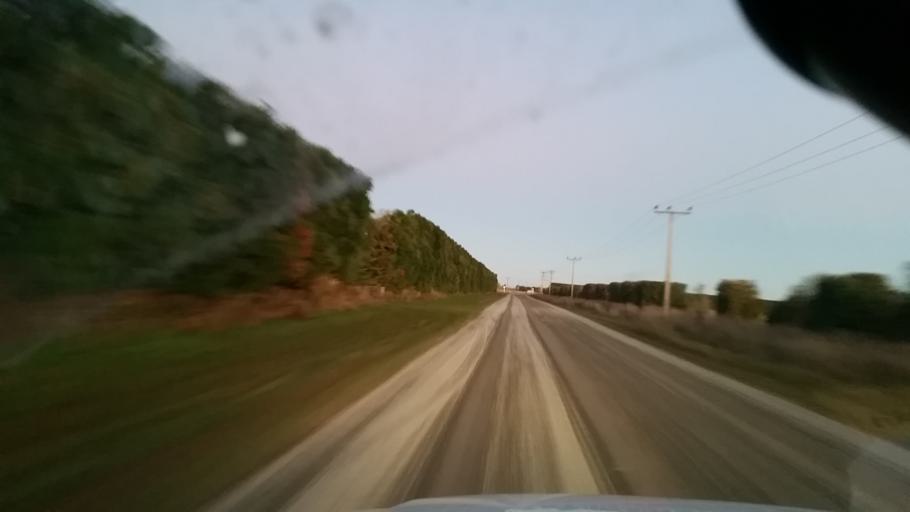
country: NZ
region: Canterbury
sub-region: Ashburton District
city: Tinwald
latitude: -43.9890
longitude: 171.6559
